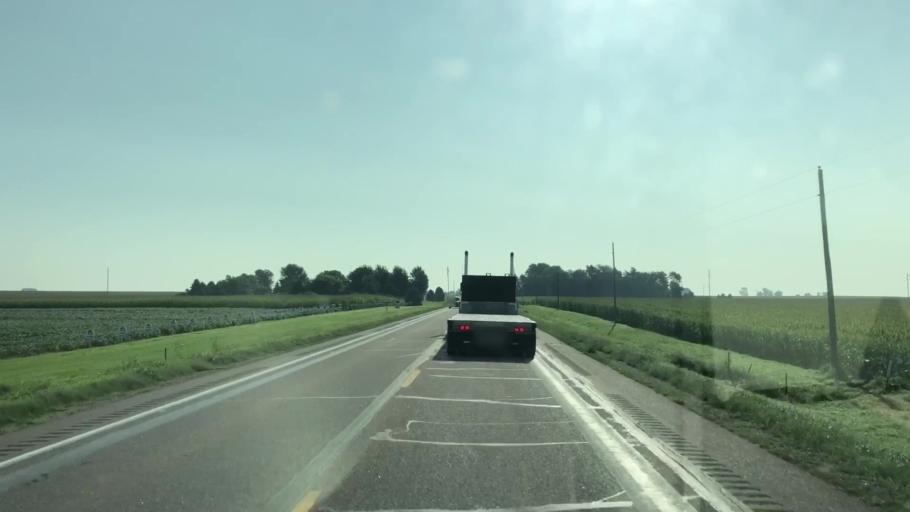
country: US
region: Iowa
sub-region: O'Brien County
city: Sheldon
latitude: 43.1863
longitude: -95.9855
